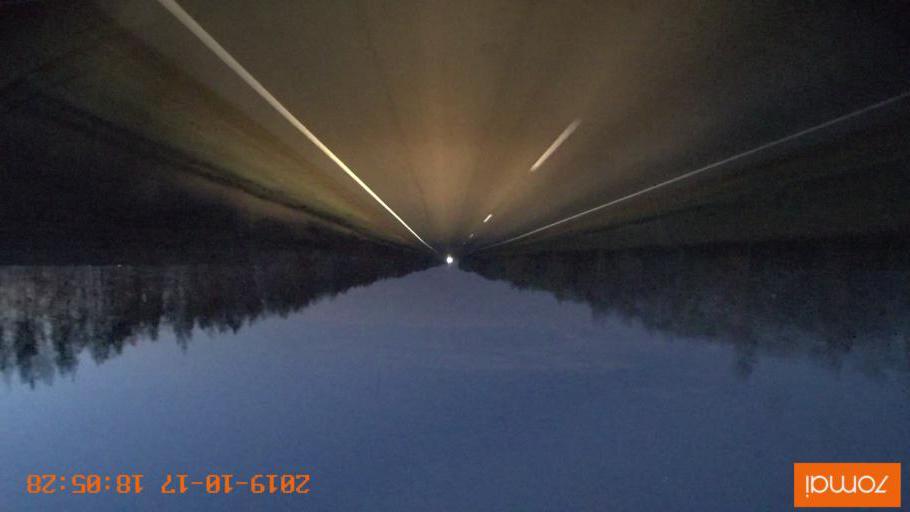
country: RU
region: Tula
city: Kurkino
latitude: 53.4661
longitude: 38.6444
